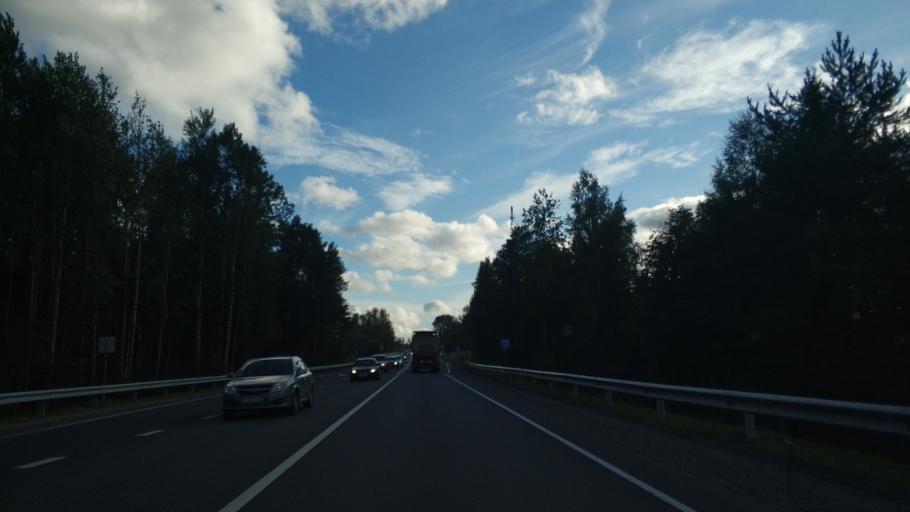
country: RU
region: Leningrad
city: Priozersk
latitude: 60.8545
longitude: 30.1519
